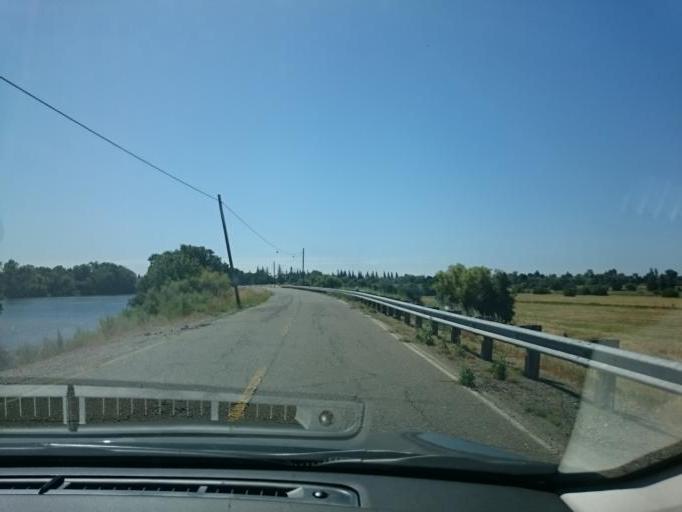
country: US
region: California
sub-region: Yolo County
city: West Sacramento
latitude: 38.5248
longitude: -121.5296
